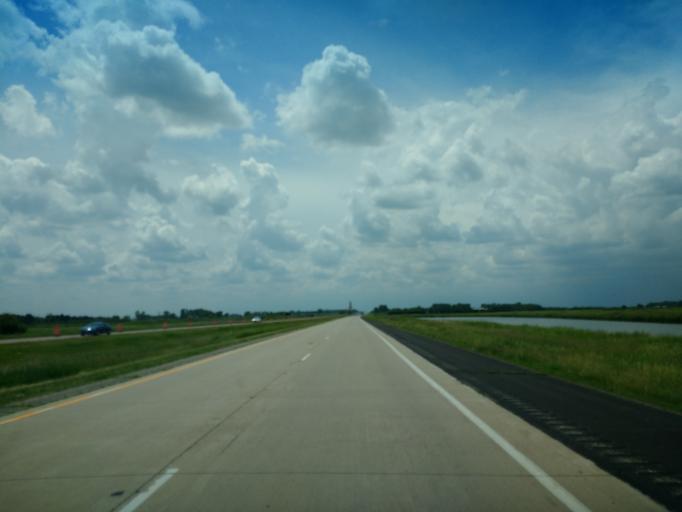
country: US
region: Minnesota
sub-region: Jackson County
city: Lakefield
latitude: 43.7863
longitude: -95.3368
